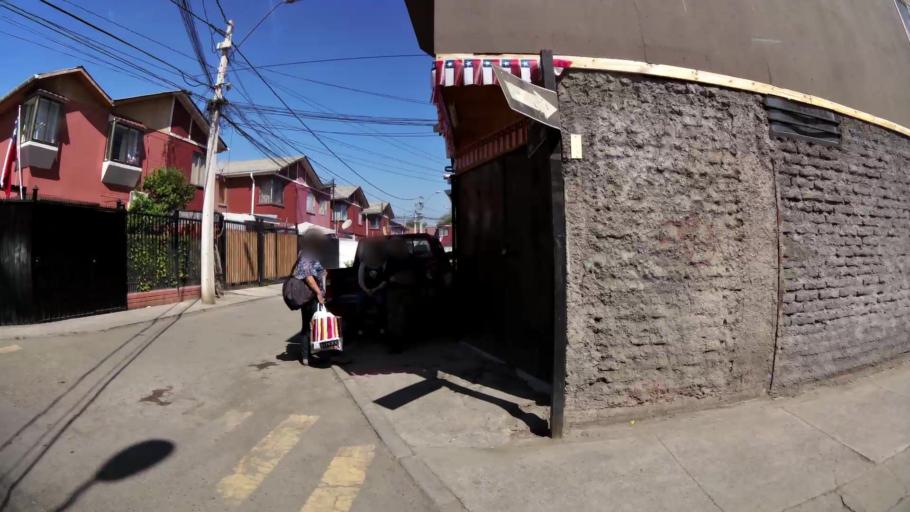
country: CL
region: Santiago Metropolitan
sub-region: Provincia de Santiago
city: Lo Prado
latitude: -33.3554
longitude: -70.7165
